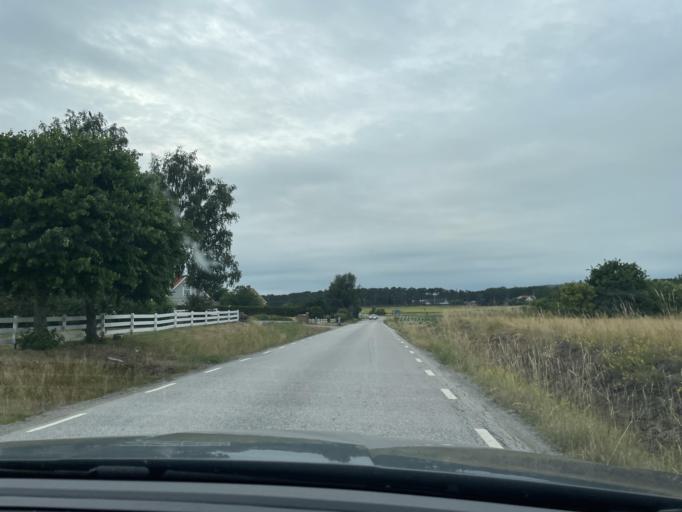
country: SE
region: Blekinge
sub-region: Solvesborgs Kommun
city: Soelvesborg
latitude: 56.0417
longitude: 14.6252
